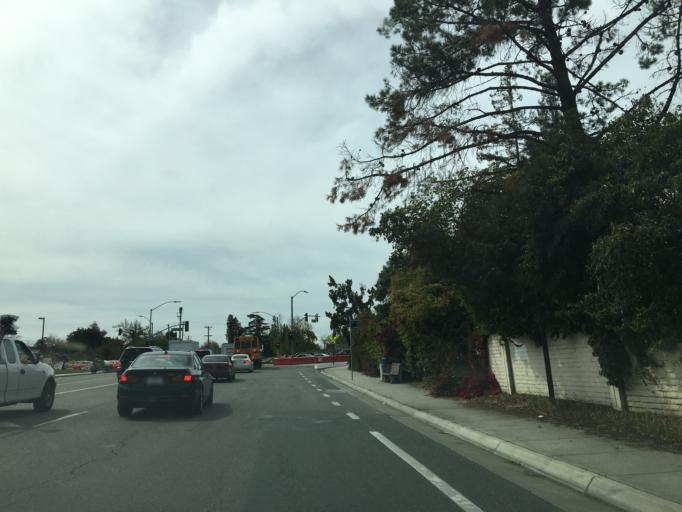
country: US
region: California
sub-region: Santa Clara County
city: Seven Trees
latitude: 37.2925
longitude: -121.8791
